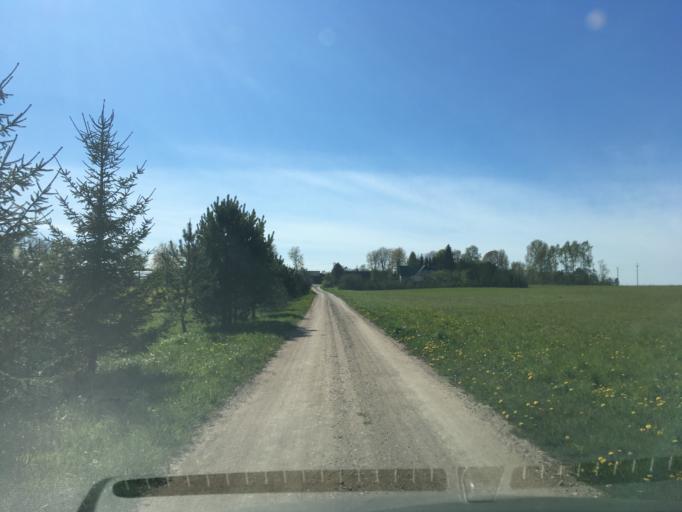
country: EE
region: Harju
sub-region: Raasiku vald
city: Arukula
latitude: 59.2647
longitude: 25.0989
